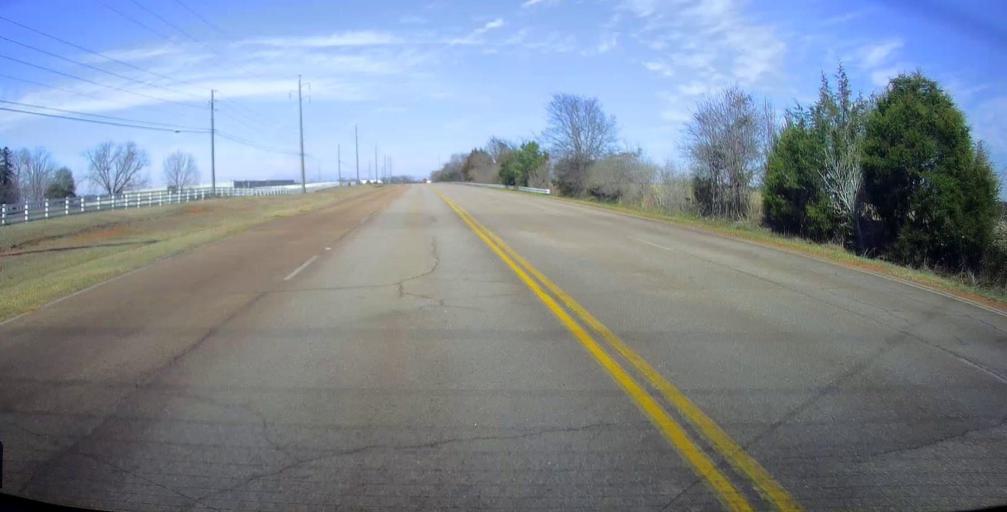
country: US
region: Georgia
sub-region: Houston County
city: Perry
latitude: 32.4840
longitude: -83.7588
